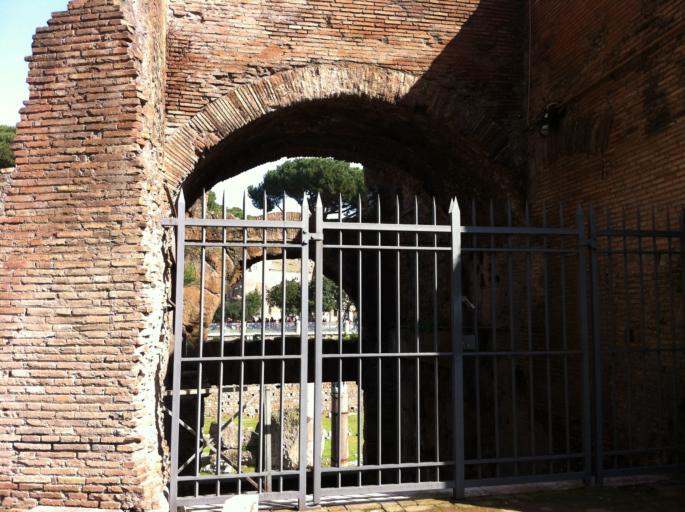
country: IT
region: Latium
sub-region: Citta metropolitana di Roma Capitale
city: Rome
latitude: 41.8938
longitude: 12.4845
